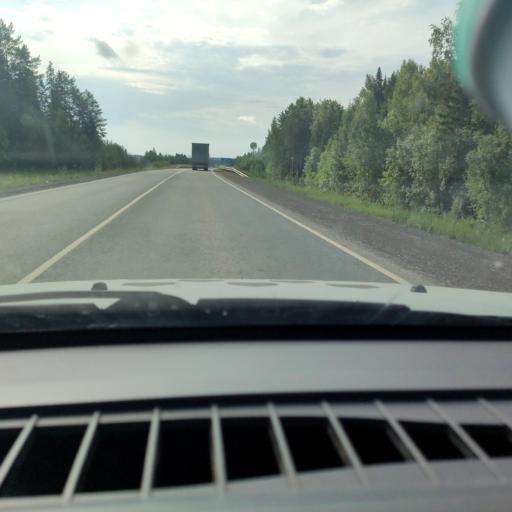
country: RU
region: Perm
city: Siva
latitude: 58.4264
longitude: 54.4515
